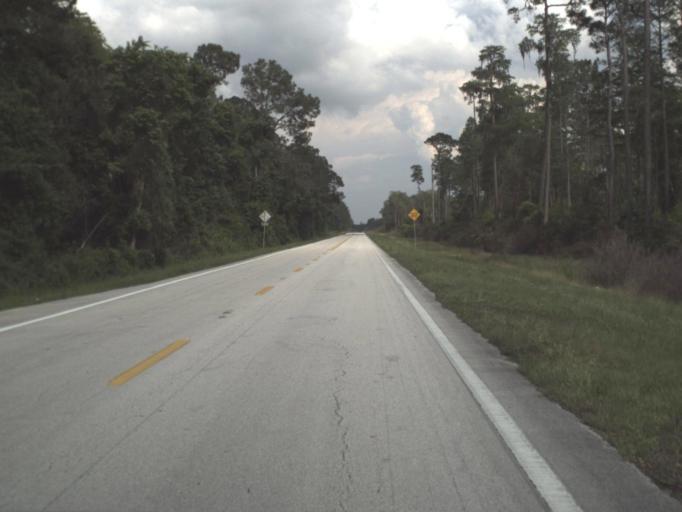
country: US
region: Florida
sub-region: Baker County
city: Macclenny
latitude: 30.5193
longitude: -82.2840
